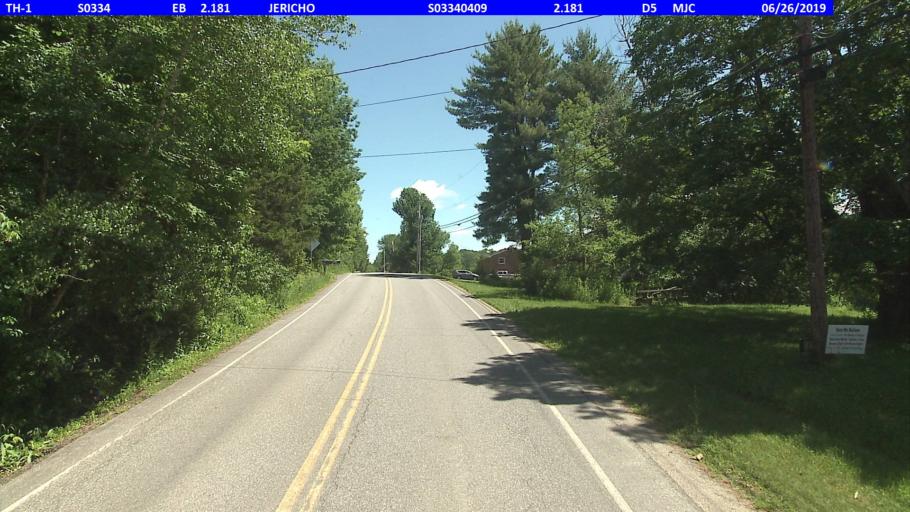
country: US
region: Vermont
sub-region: Chittenden County
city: Jericho
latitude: 44.4626
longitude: -72.9796
